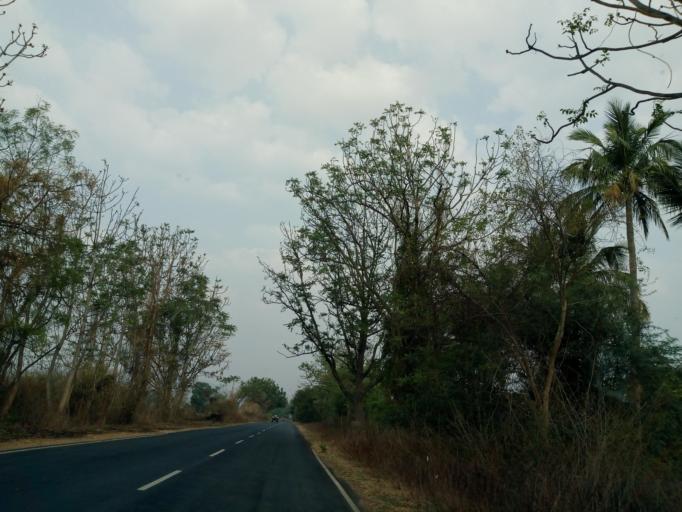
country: IN
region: Andhra Pradesh
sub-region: Prakasam
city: Diguvametta
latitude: 15.3780
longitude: 78.8614
